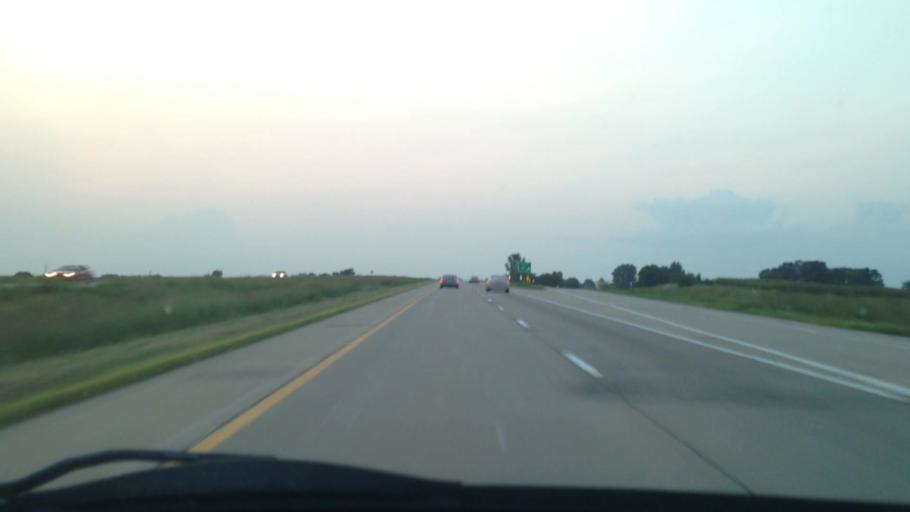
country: US
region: Iowa
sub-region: Benton County
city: Urbana
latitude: 42.3082
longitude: -91.9728
